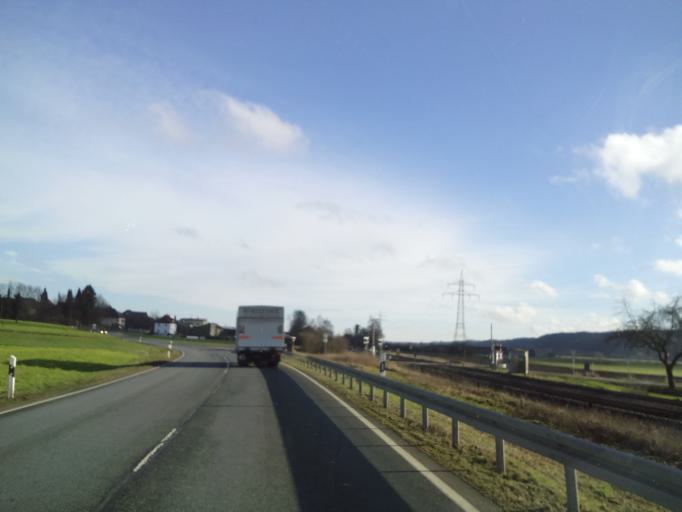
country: DE
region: Bavaria
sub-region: Upper Franconia
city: Altenkunstadt
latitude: 50.1236
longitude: 11.3115
